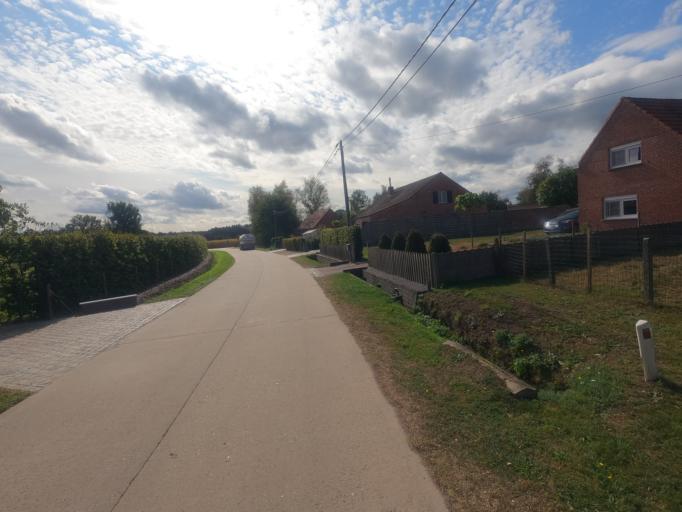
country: BE
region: Flanders
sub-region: Provincie Antwerpen
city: Lille
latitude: 51.2565
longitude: 4.8241
